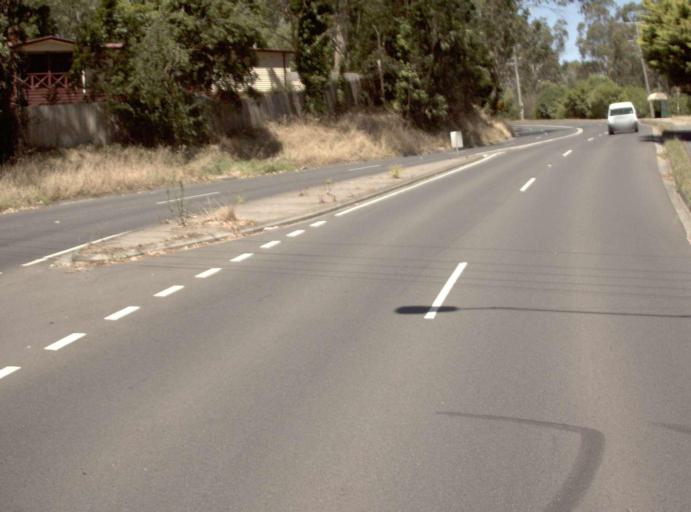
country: AU
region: Victoria
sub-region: Yarra Ranges
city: Tremont
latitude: -37.9054
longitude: 145.3373
